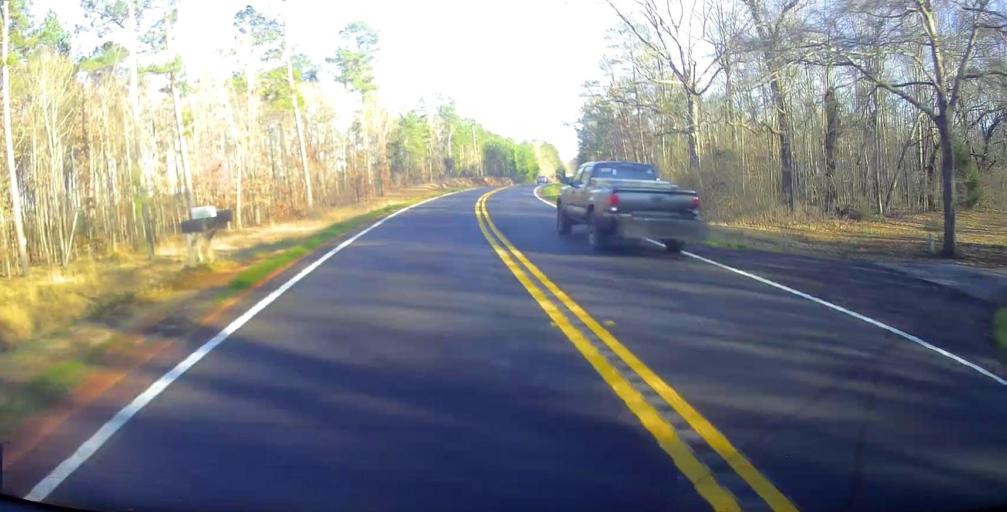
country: US
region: Georgia
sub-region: Meriwether County
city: Greenville
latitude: 32.9122
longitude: -84.7306
